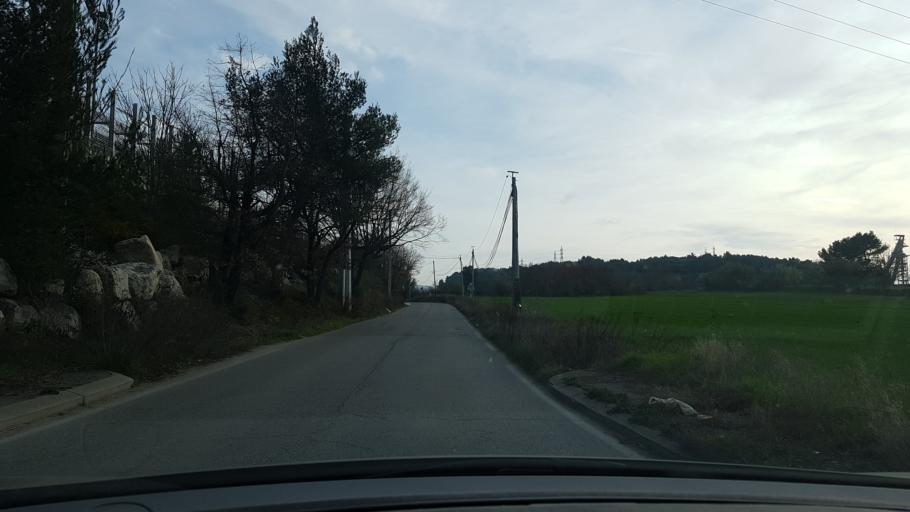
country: FR
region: Provence-Alpes-Cote d'Azur
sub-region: Departement des Bouches-du-Rhone
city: Gardanne
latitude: 43.4716
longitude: 5.4812
